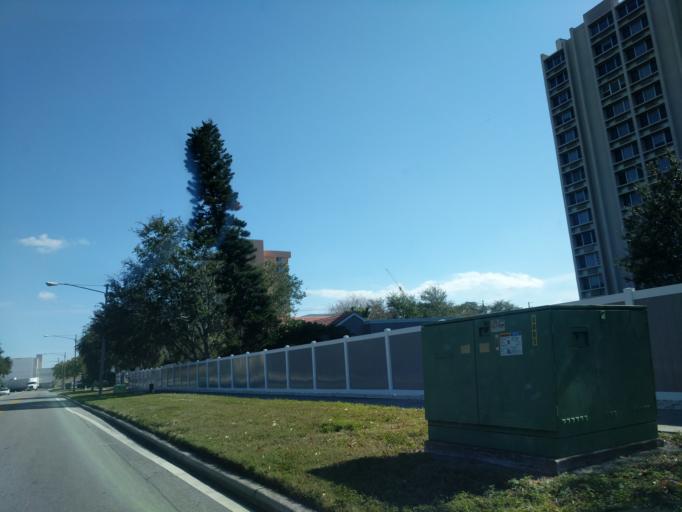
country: US
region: Florida
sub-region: Pinellas County
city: Saint Petersburg
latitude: 27.7739
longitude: -82.6497
